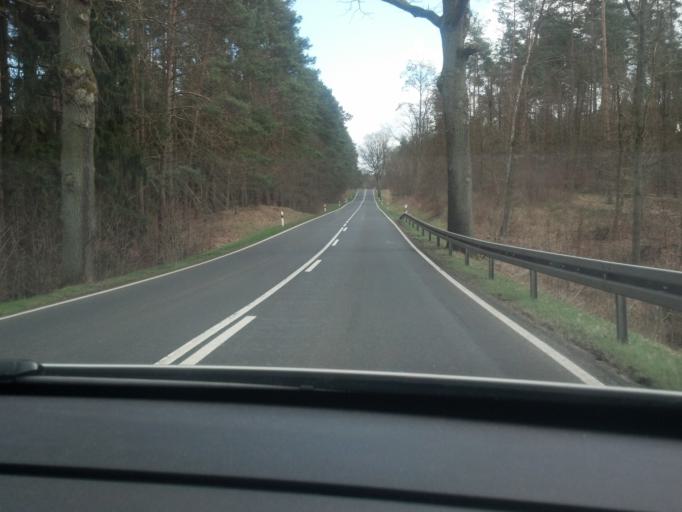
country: DE
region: Mecklenburg-Vorpommern
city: Carpin
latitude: 53.3664
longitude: 13.1979
